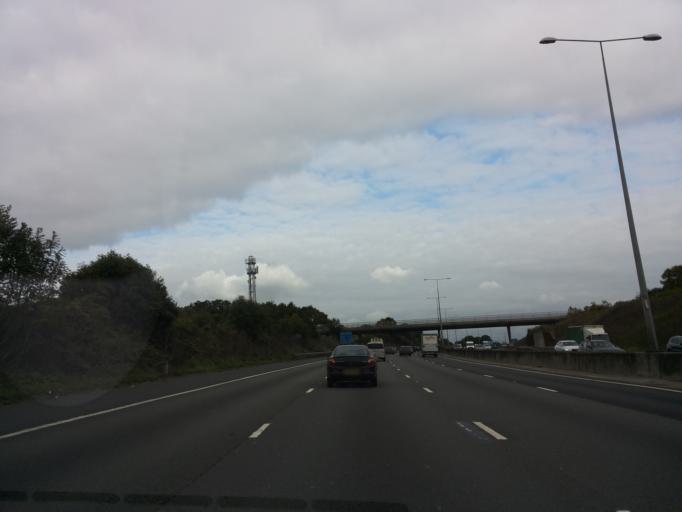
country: GB
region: England
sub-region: Hertfordshire
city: Chorleywood
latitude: 51.6691
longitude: -0.4902
